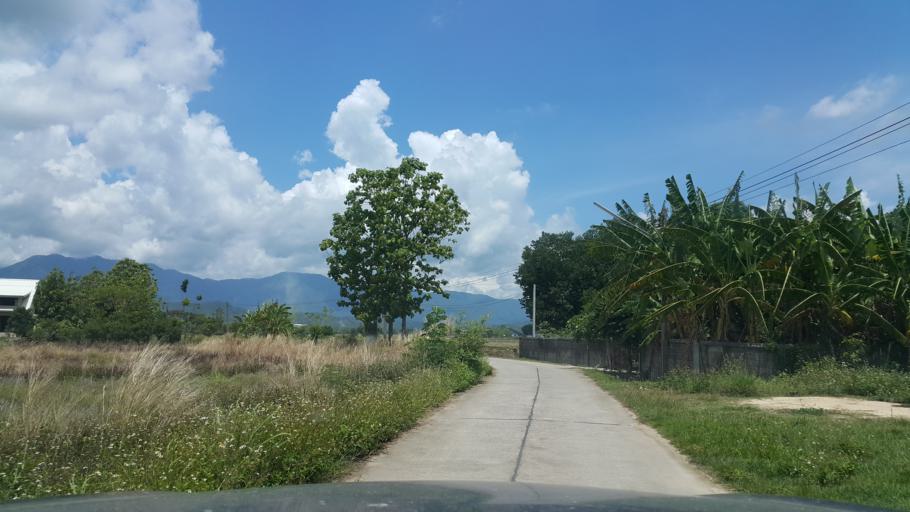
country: TH
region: Phayao
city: Phayao
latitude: 19.1808
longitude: 99.8464
